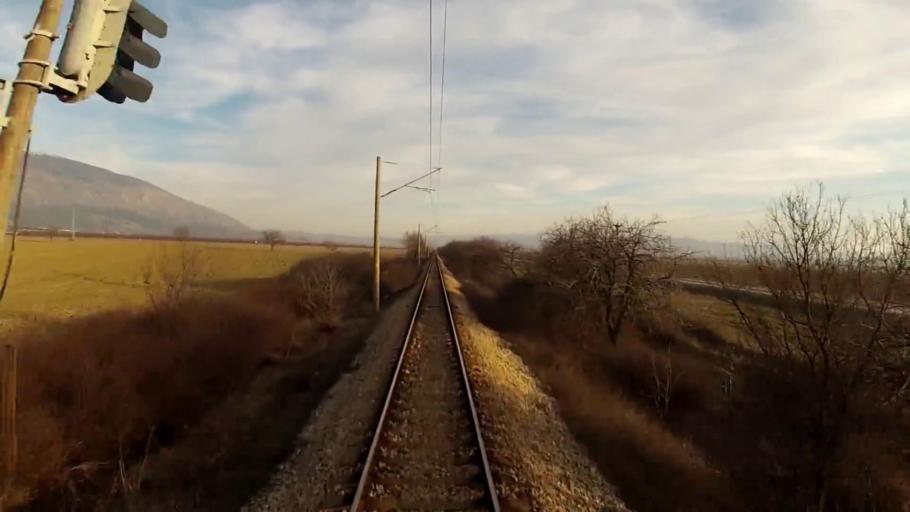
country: BG
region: Plovdiv
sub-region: Obshtina Karlovo
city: Karlovo
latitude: 42.6354
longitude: 24.7650
